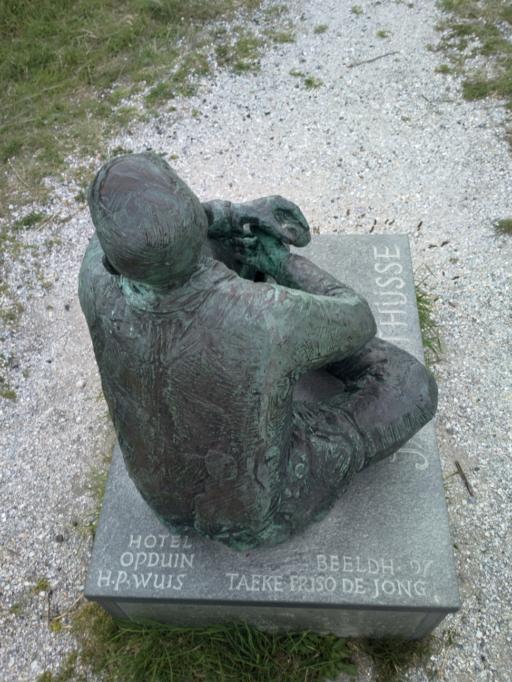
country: NL
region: North Holland
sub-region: Gemeente Texel
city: Den Burg
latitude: 53.0810
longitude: 4.7480
